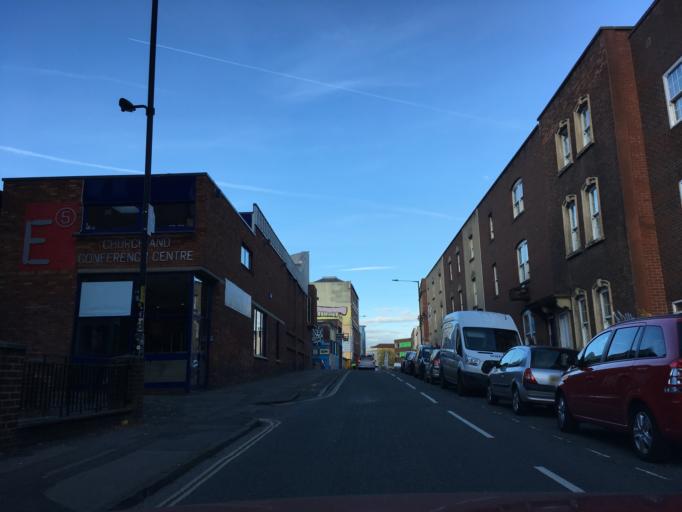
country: GB
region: England
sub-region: Bristol
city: Bristol
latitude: 51.4618
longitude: -2.5916
